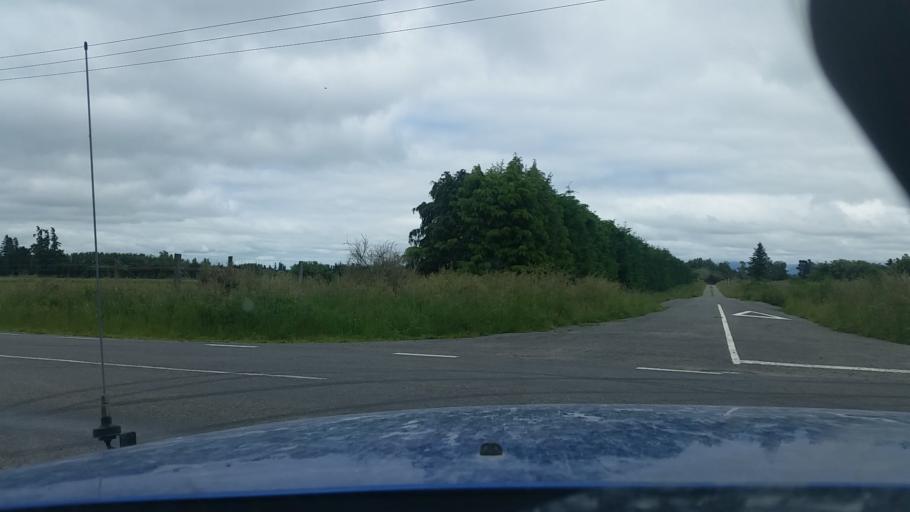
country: NZ
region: Canterbury
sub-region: Ashburton District
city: Methven
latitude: -43.7905
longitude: 171.4280
